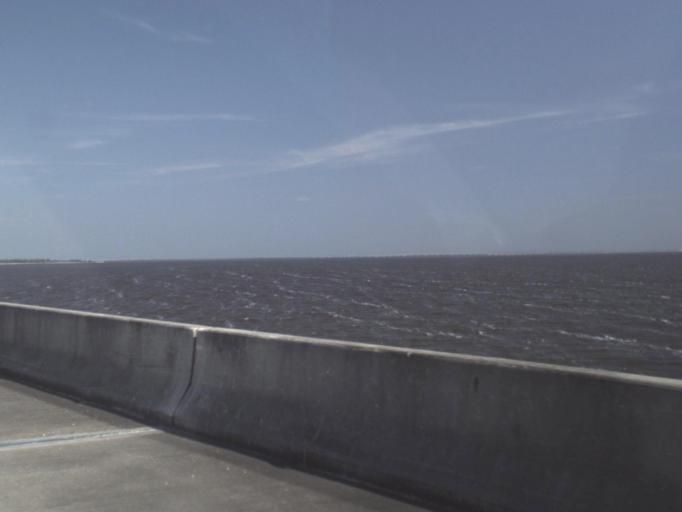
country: US
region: Florida
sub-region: Franklin County
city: Eastpoint
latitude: 29.7315
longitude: -84.9295
